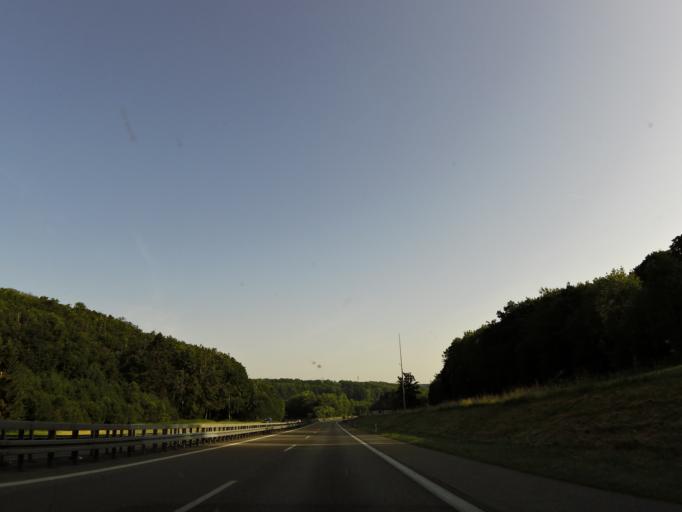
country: DE
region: Baden-Wuerttemberg
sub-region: Regierungsbezirk Stuttgart
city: Hohenstadt
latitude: 48.5401
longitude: 9.6492
